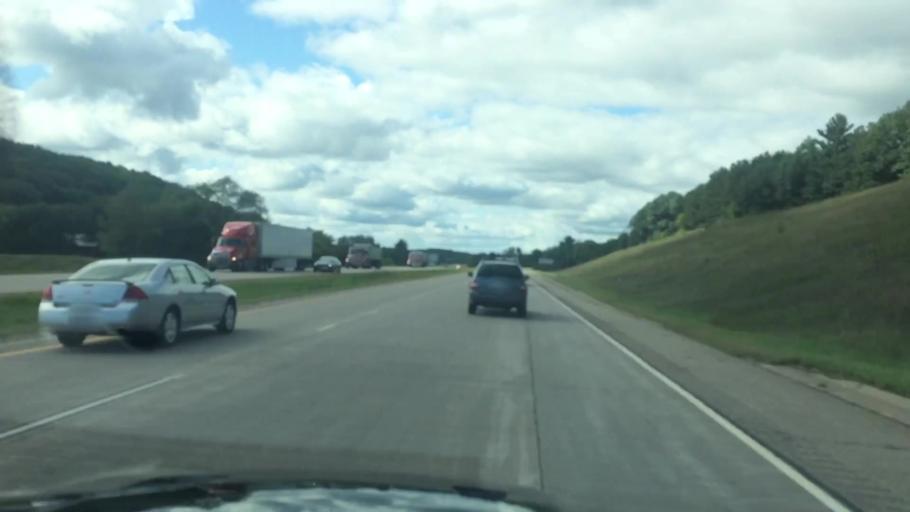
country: US
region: Wisconsin
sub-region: Waupaca County
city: Waupaca
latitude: 44.3406
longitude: -89.0744
